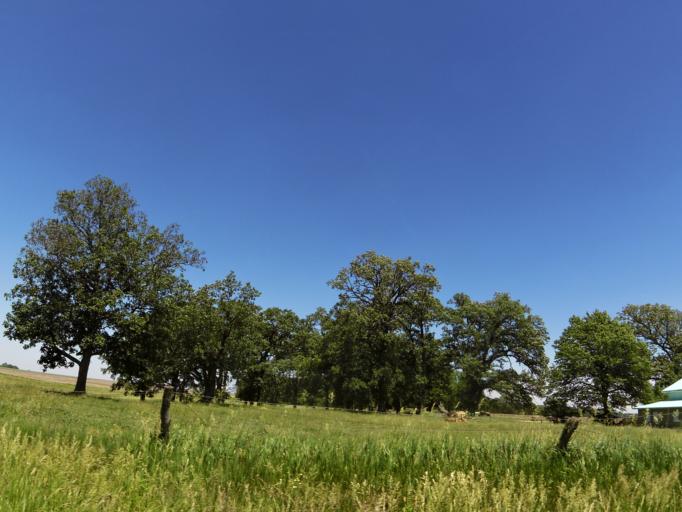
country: US
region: Illinois
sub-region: Iroquois County
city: Milford
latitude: 40.6850
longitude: -87.7552
